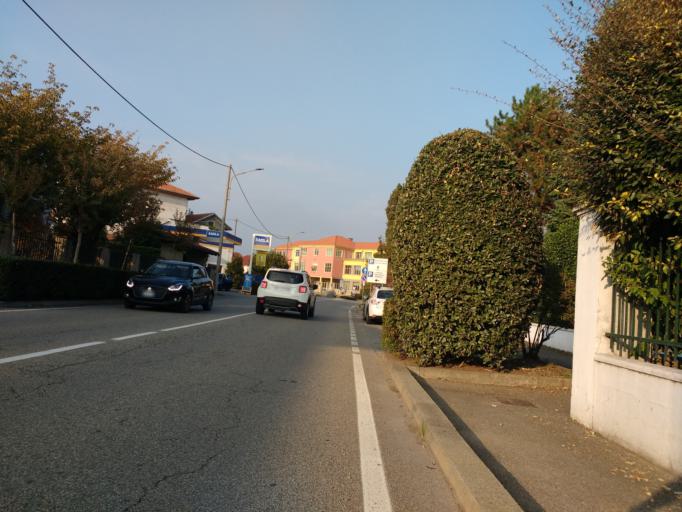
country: IT
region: Piedmont
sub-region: Provincia di Biella
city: Candelo
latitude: 45.5409
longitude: 8.1111
